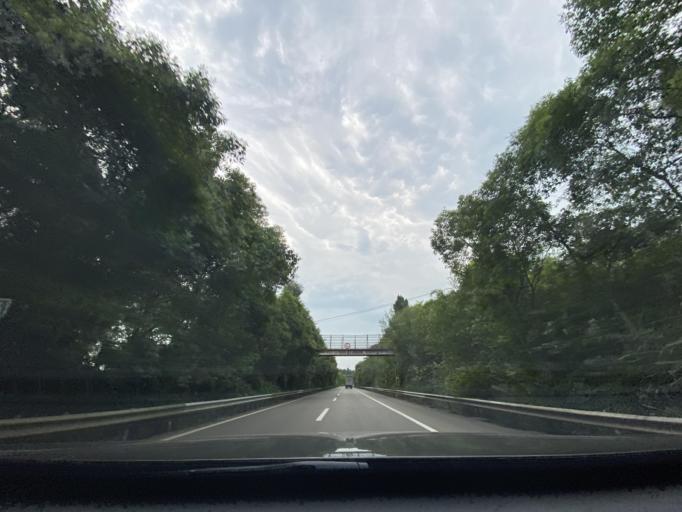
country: CN
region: Sichuan
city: Neijiang
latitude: 29.6799
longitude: 104.9591
